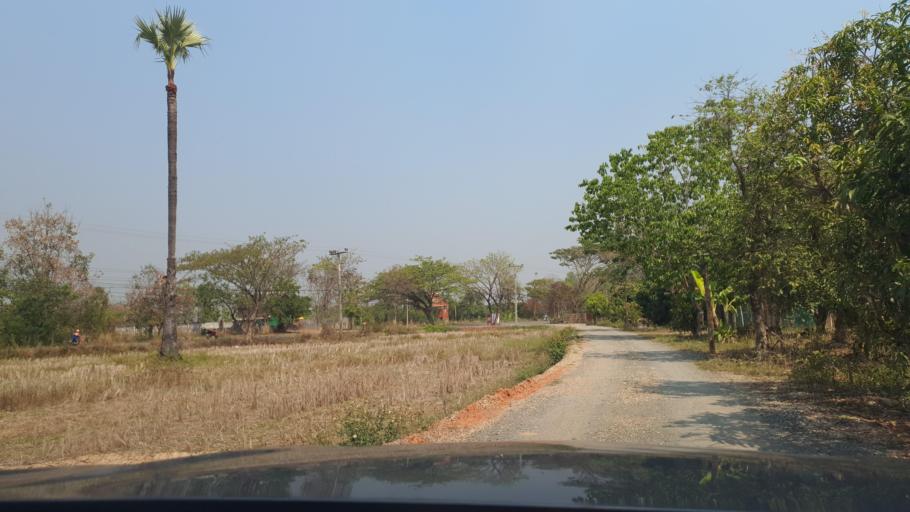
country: TH
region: Lamphun
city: Ban Thi
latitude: 18.6634
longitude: 99.1335
